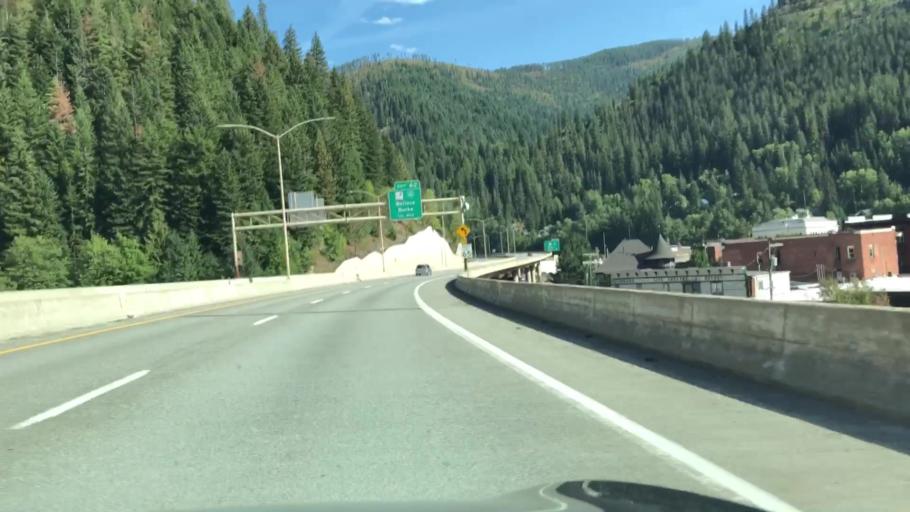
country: US
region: Idaho
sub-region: Shoshone County
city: Wallace
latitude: 47.4744
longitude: -115.9252
